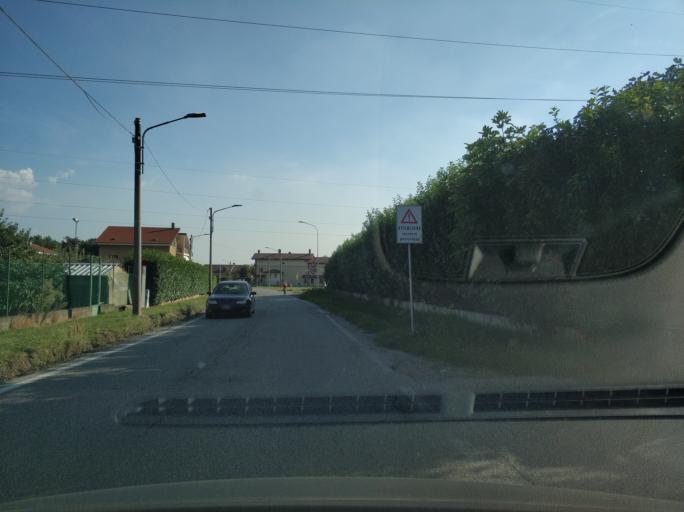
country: IT
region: Piedmont
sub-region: Provincia di Torino
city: San Maurizio
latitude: 45.2105
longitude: 7.6295
